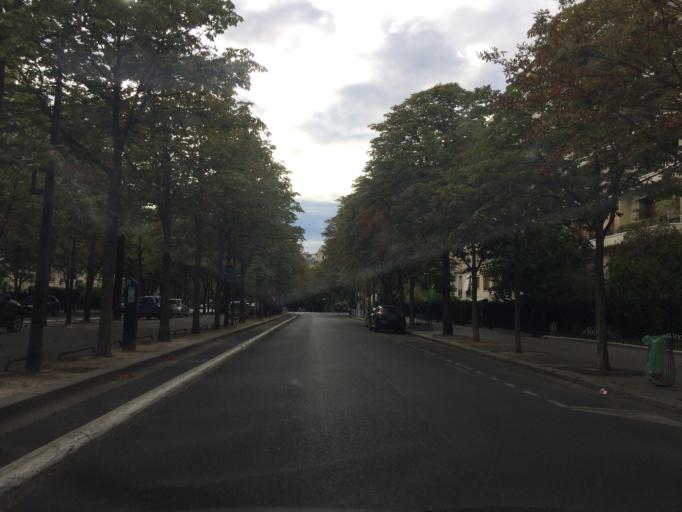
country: FR
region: Ile-de-France
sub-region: Departement des Hauts-de-Seine
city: Neuilly-sur-Seine
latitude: 48.8642
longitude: 2.2768
